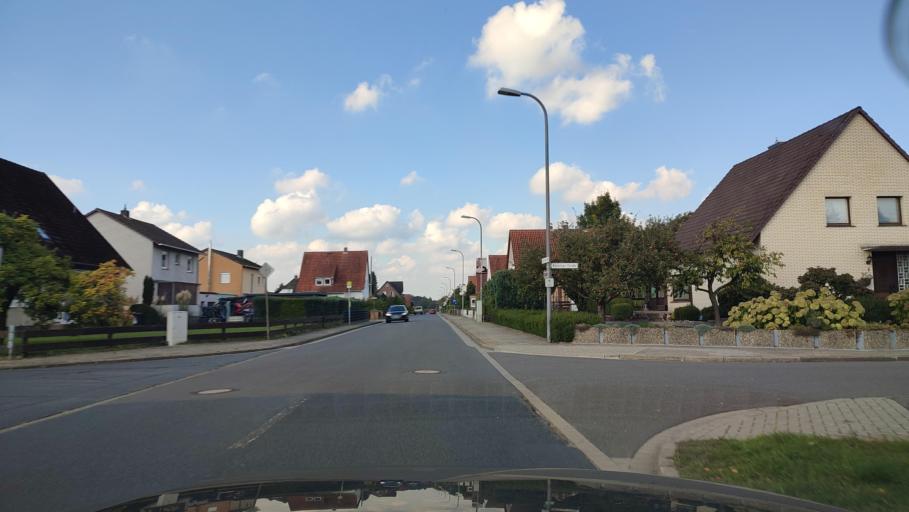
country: DE
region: Lower Saxony
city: Bomlitz
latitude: 52.8995
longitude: 9.6712
